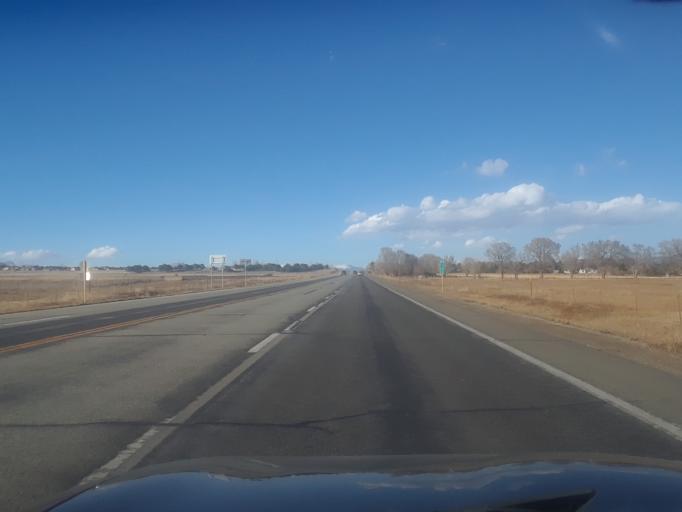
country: US
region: Colorado
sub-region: Chaffee County
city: Salida
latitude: 38.5333
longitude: -106.0797
